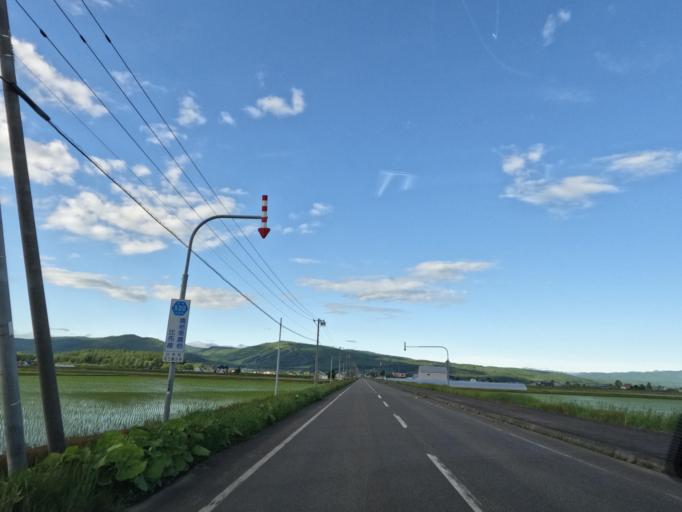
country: JP
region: Hokkaido
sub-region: Asahikawa-shi
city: Asahikawa
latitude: 43.8897
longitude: 142.4652
